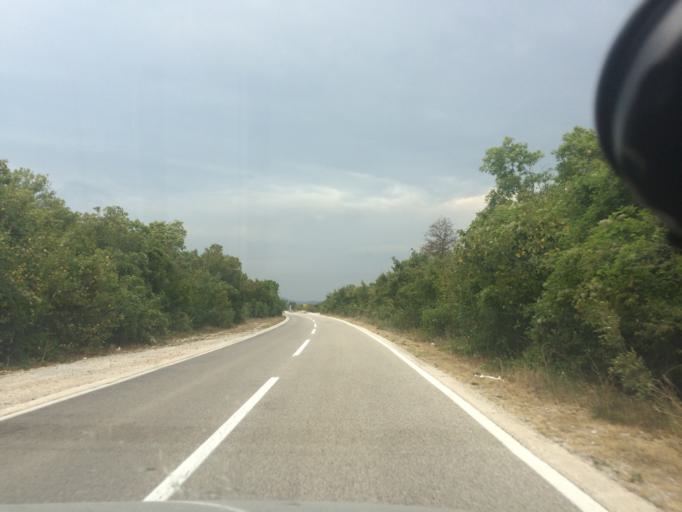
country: ME
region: Kotor
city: Risan
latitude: 42.5813
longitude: 18.6872
